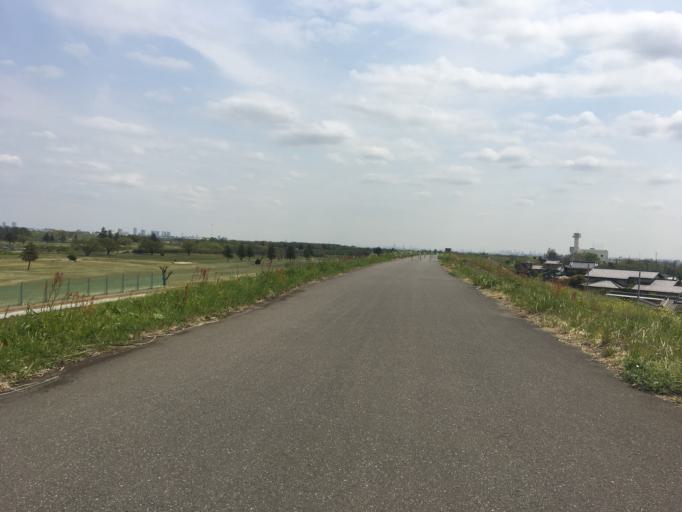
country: JP
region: Saitama
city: Shiki
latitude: 35.8760
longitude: 139.5700
